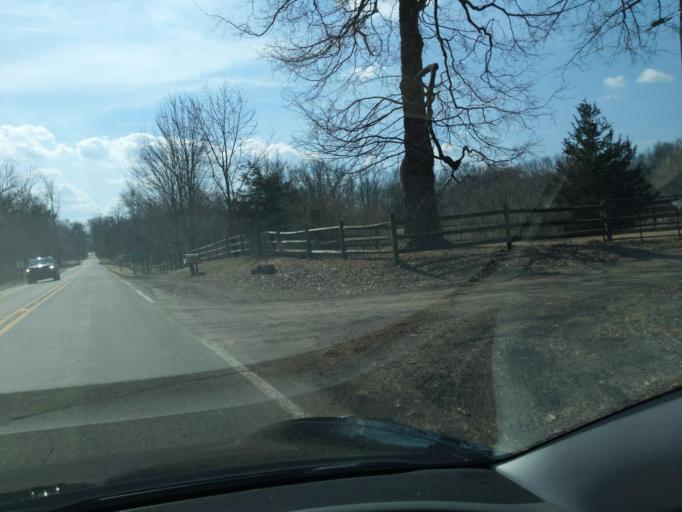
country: US
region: Michigan
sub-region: Livingston County
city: Pinckney
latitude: 42.4324
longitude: -84.0581
